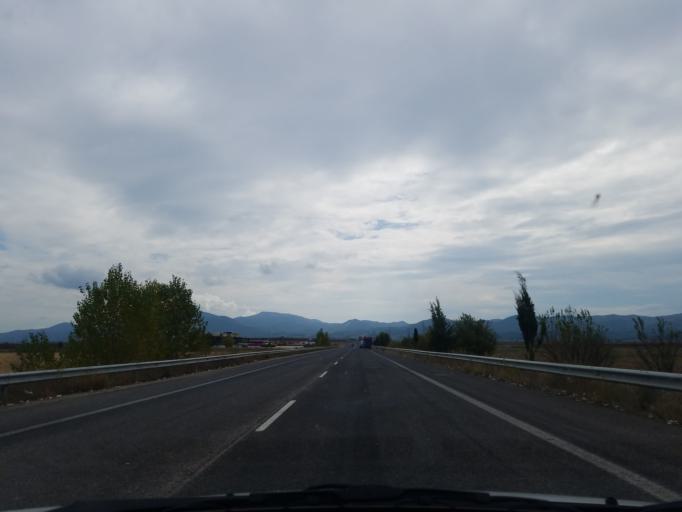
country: GR
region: Central Greece
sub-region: Nomos Fthiotidos
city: Omvriaki
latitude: 39.0702
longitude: 22.3222
